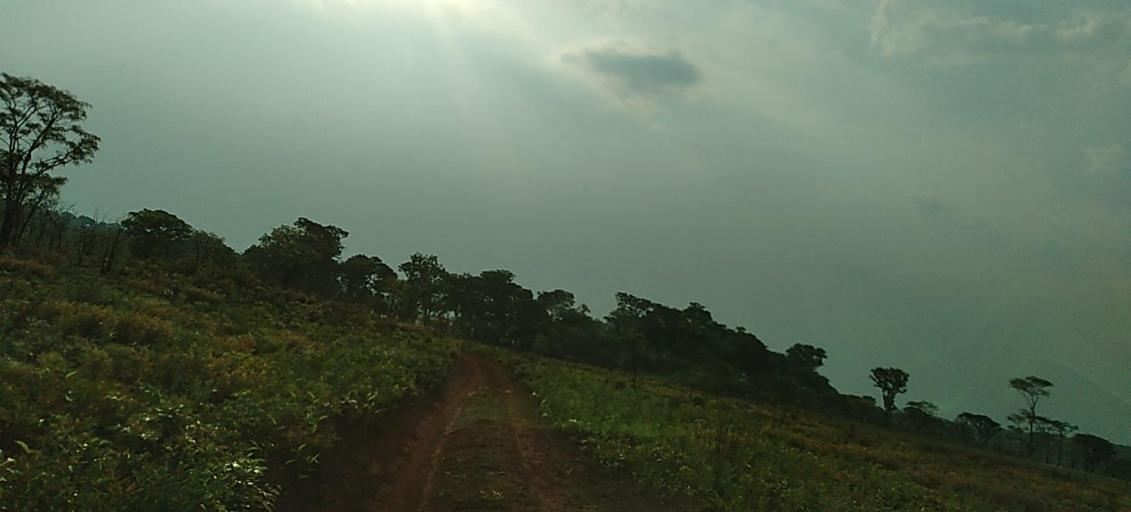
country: ZM
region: North-Western
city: Solwezi
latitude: -12.0466
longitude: 26.0619
